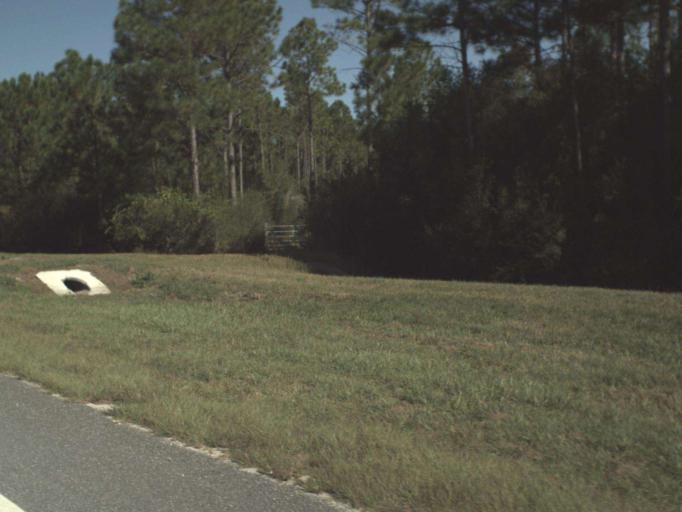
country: US
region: Florida
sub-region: Walton County
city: Seaside
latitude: 30.3256
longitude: -86.0504
